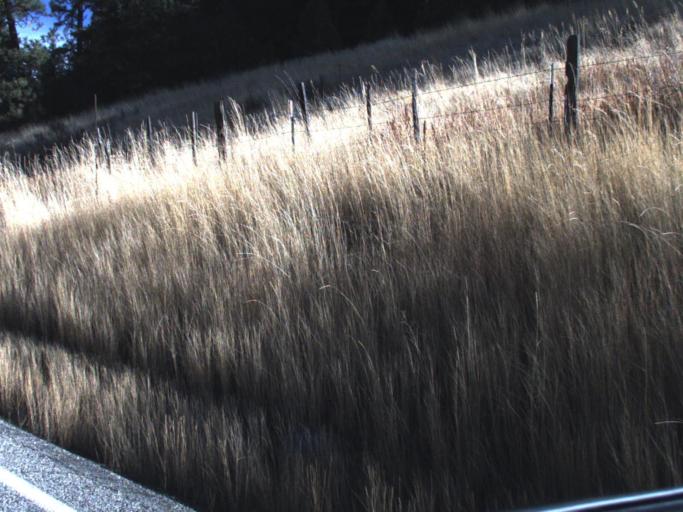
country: US
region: Washington
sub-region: Ferry County
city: Republic
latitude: 48.7411
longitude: -118.6603
